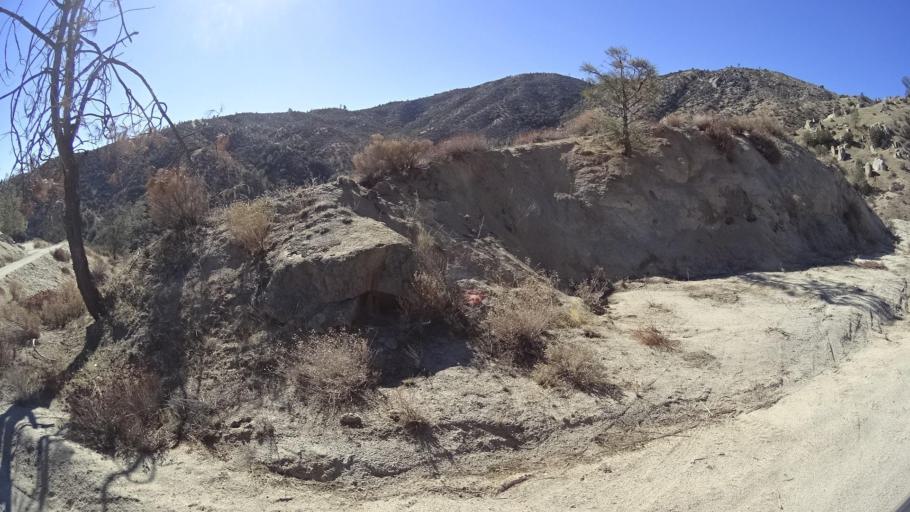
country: US
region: California
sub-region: Kern County
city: Wofford Heights
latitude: 35.7004
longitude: -118.4837
